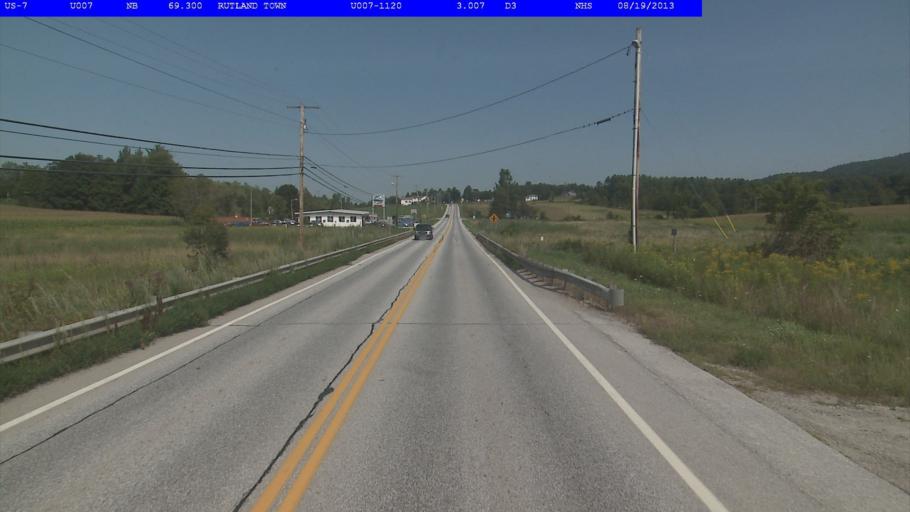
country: US
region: Vermont
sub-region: Rutland County
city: Rutland
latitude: 43.6539
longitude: -72.9866
